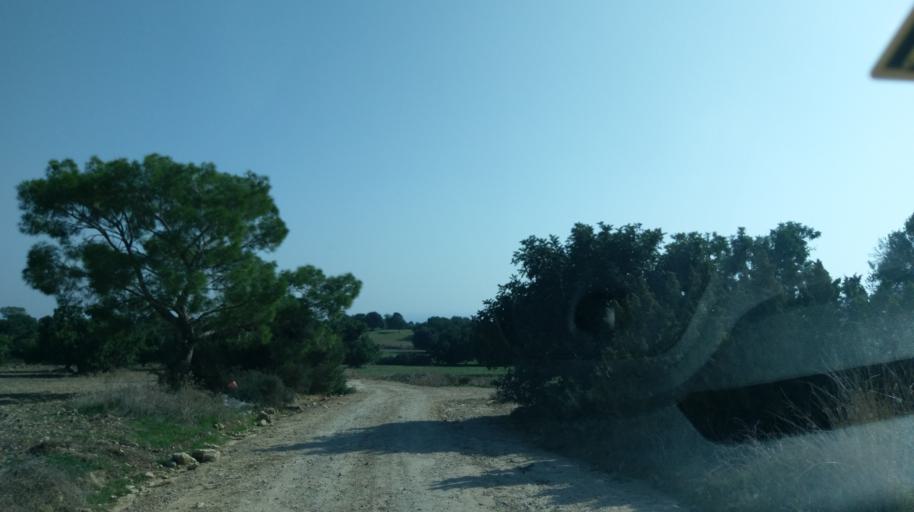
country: CY
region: Ammochostos
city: Leonarisso
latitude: 35.4854
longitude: 34.2202
